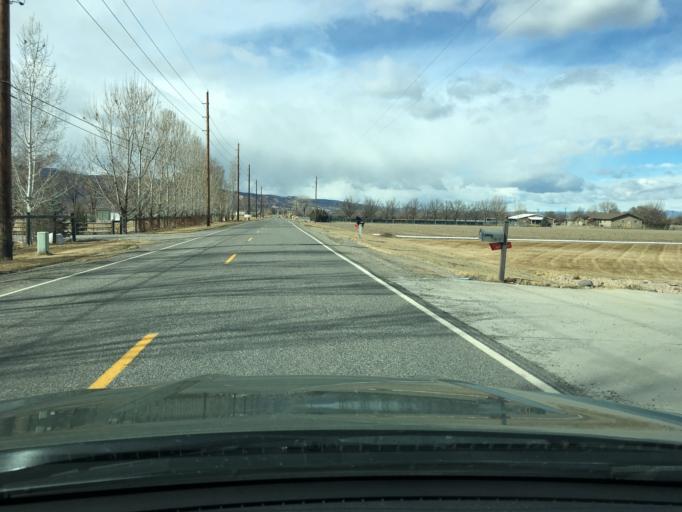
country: US
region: Colorado
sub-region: Mesa County
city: Redlands
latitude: 39.1209
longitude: -108.6224
